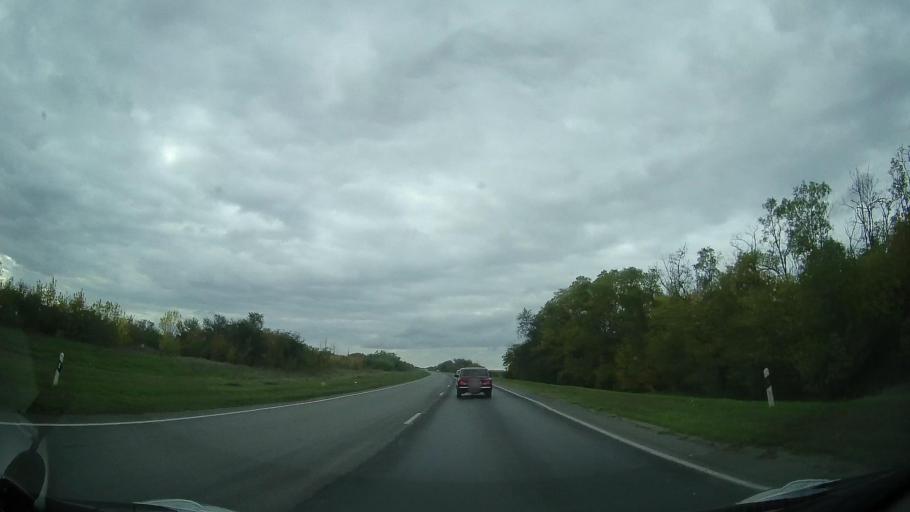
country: RU
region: Rostov
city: Yegorlykskaya
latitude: 46.5457
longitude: 40.7634
